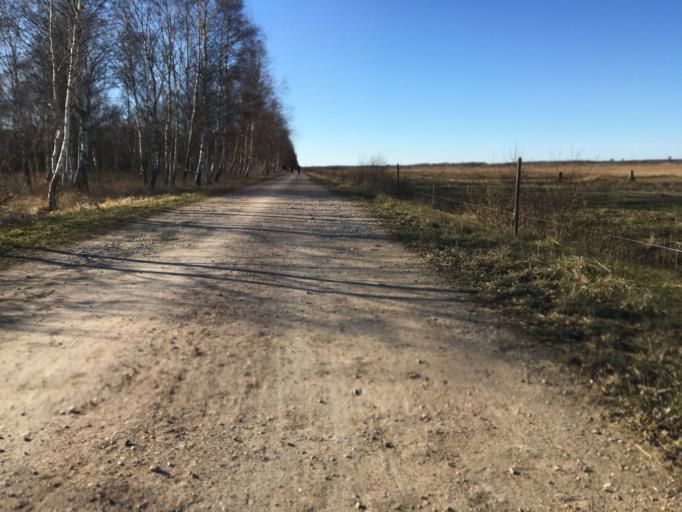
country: DK
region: Capital Region
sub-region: Tarnby Kommune
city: Tarnby
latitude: 55.5956
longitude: 12.5646
